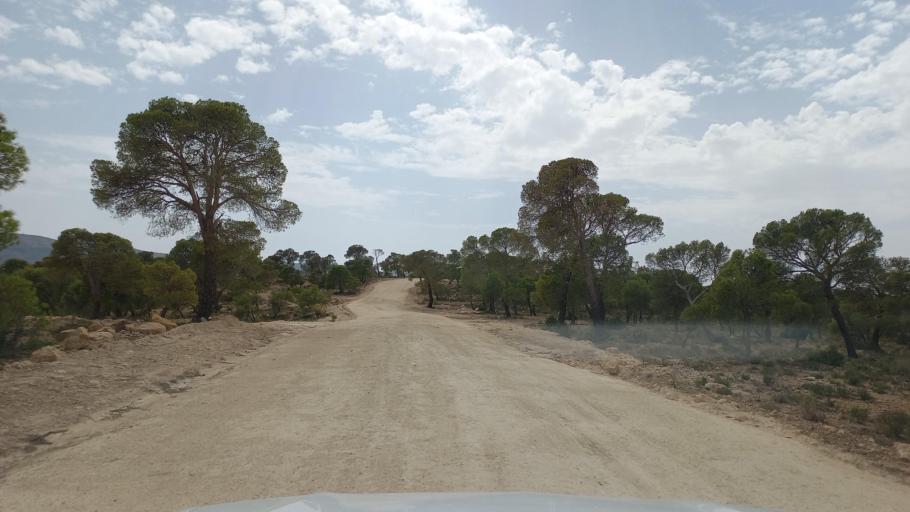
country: TN
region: Al Qasrayn
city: Kasserine
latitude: 35.3783
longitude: 8.8691
